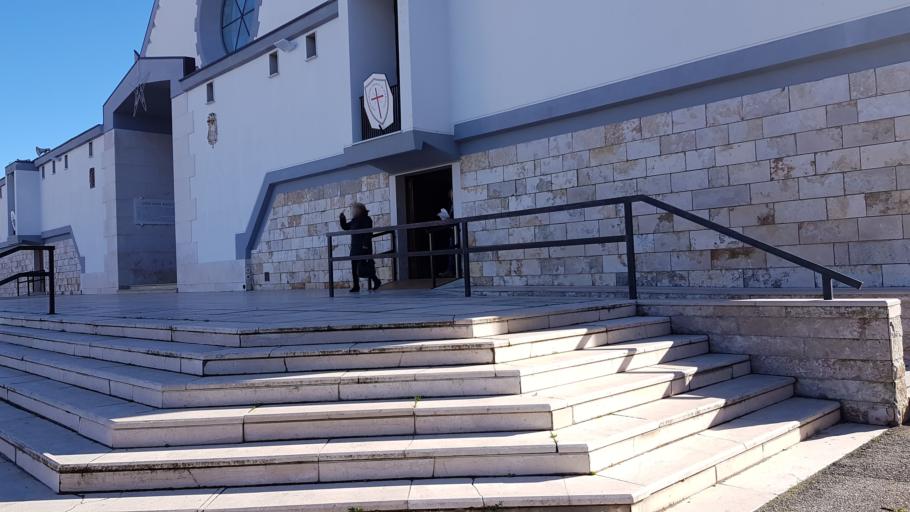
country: IT
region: Apulia
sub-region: Provincia di Foggia
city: Carapelle
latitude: 41.3816
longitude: 15.6405
